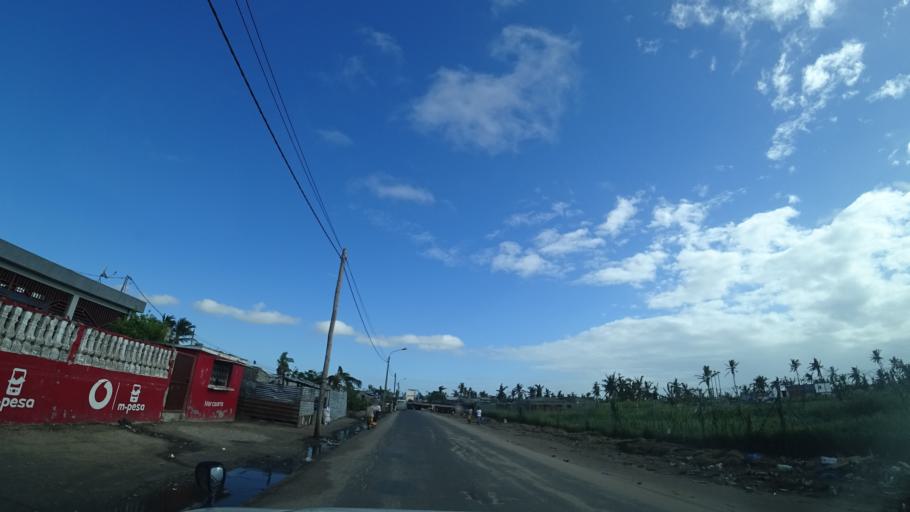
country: MZ
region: Sofala
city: Beira
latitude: -19.7920
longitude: 34.8883
